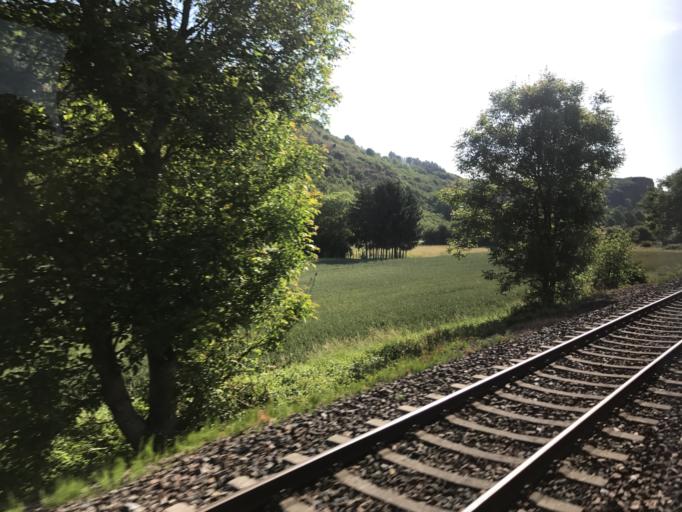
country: DE
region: Rheinland-Pfalz
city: Staudernheim
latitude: 49.7809
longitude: 7.6806
